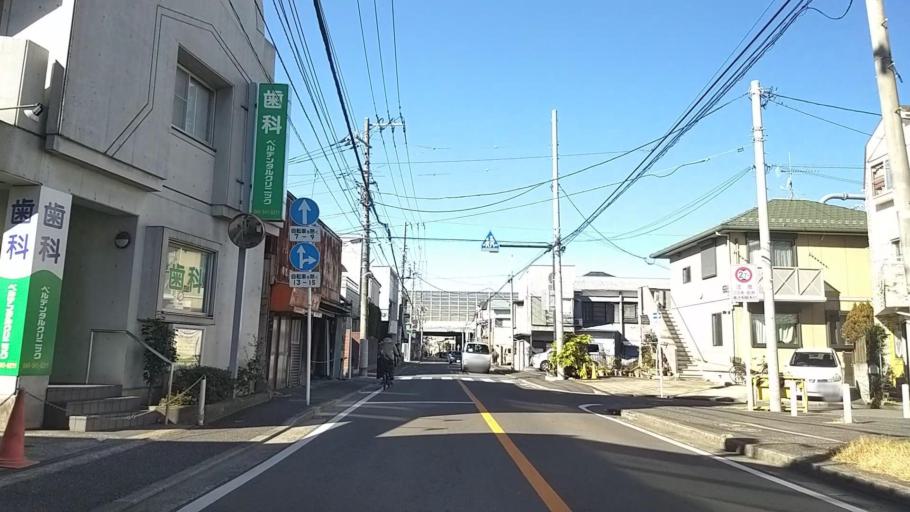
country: JP
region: Kanagawa
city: Yokohama
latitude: 35.4618
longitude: 139.5908
